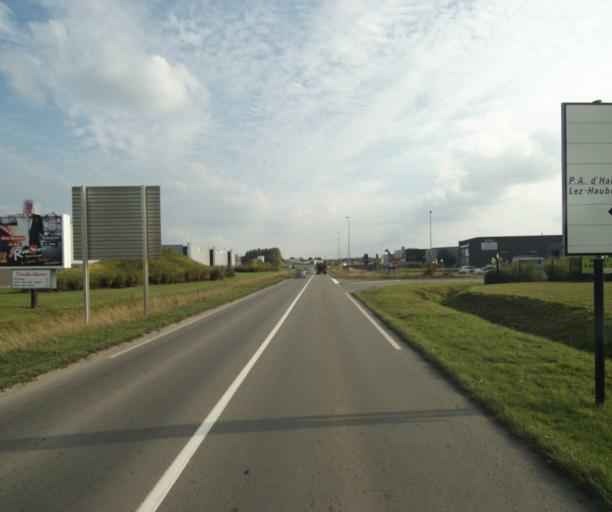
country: FR
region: Nord-Pas-de-Calais
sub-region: Departement du Nord
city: Hallennes-lez-Haubourdin
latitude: 50.6062
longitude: 2.9568
